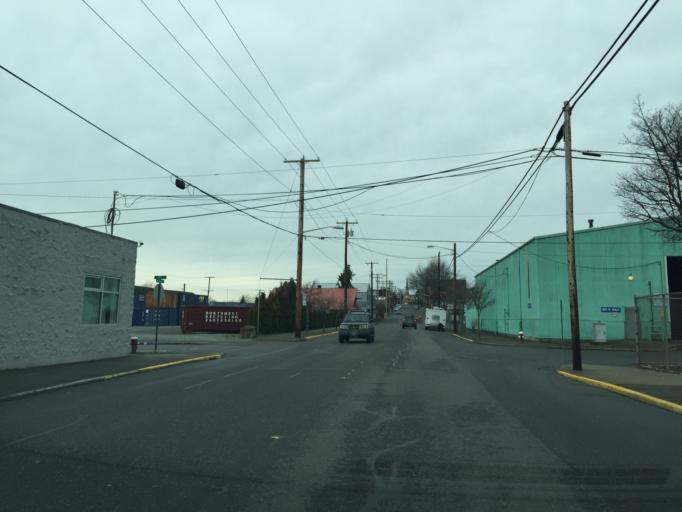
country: US
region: Washington
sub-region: Whatcom County
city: Bellingham
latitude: 48.7540
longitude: -122.4857
